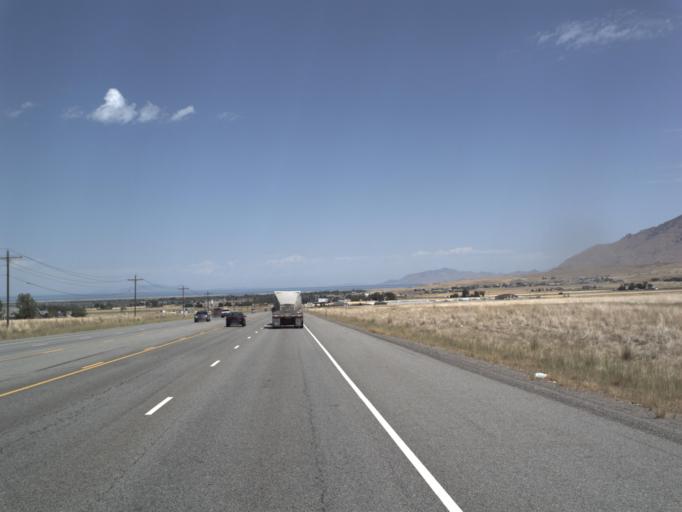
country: US
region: Utah
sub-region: Tooele County
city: Erda
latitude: 40.5812
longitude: -112.2937
